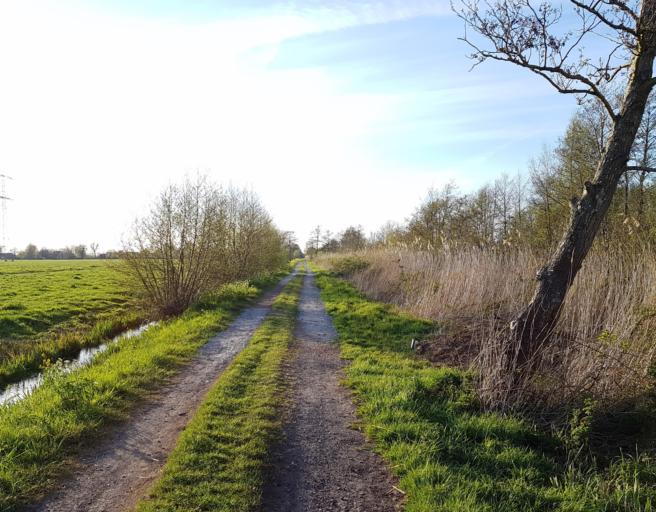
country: NL
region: South Holland
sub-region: Gemeente Gouda
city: Gouda
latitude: 51.9644
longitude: 4.7069
